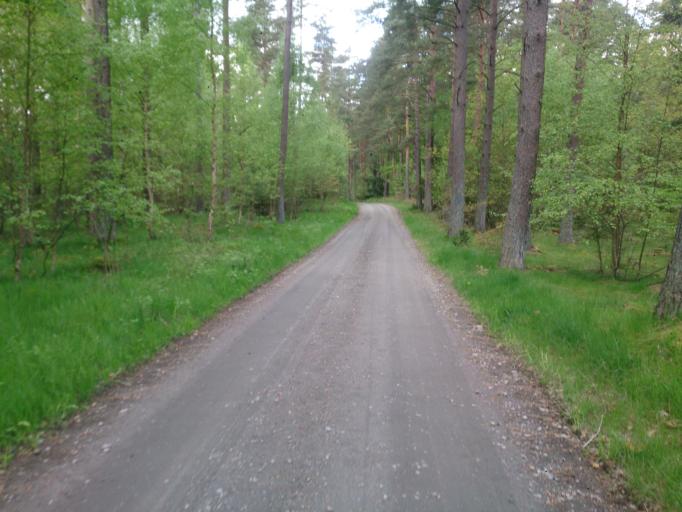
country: SE
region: Skane
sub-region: Sjobo Kommun
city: Sjoebo
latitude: 55.5600
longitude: 13.6951
